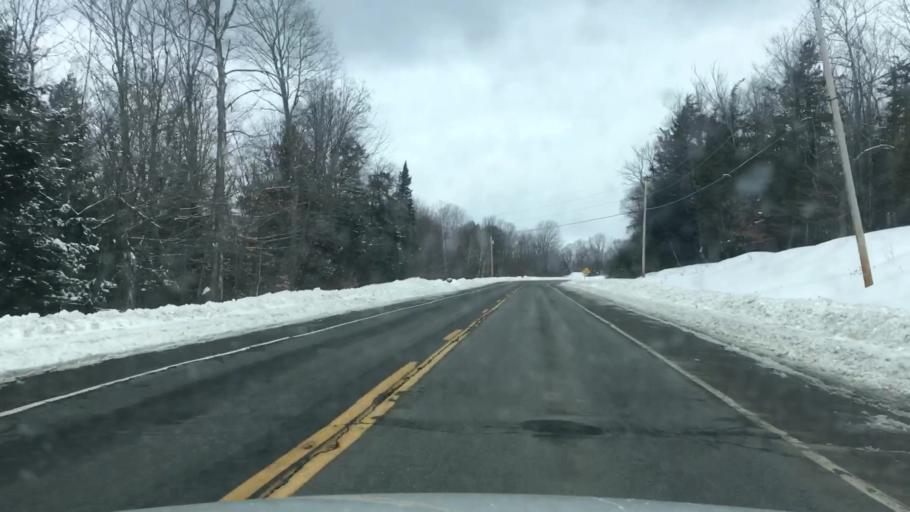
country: US
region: Maine
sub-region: Somerset County
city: Cornville
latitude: 44.8148
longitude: -69.7069
